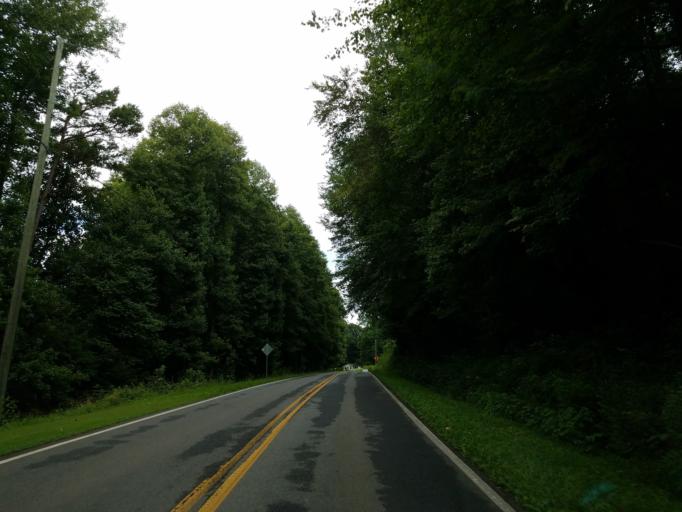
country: US
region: Georgia
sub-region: Gilmer County
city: Ellijay
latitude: 34.6708
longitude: -84.3567
